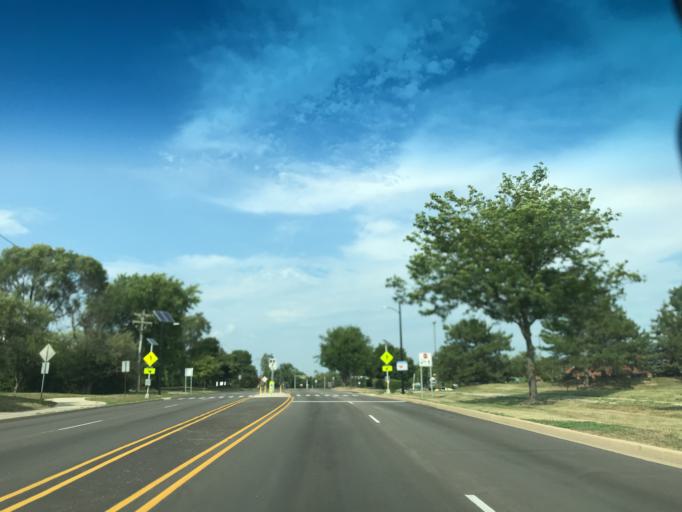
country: US
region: Michigan
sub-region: Washtenaw County
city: Ann Arbor
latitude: 42.2532
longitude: -83.7539
